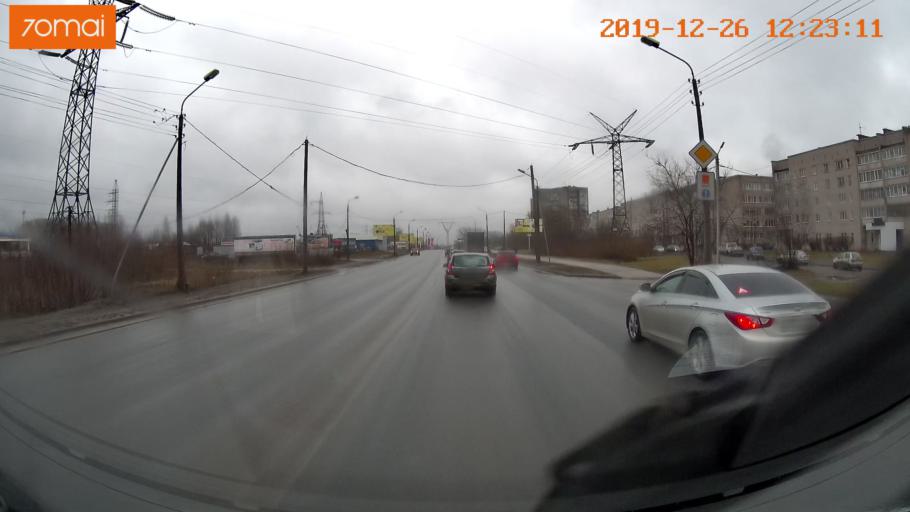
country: RU
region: Vologda
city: Tonshalovo
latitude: 59.1498
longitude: 37.9540
